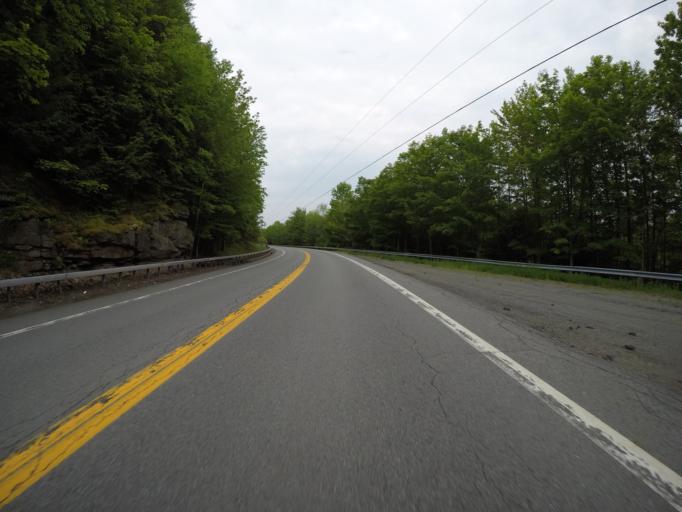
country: US
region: New York
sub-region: Sullivan County
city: Livingston Manor
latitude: 42.0745
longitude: -74.8416
